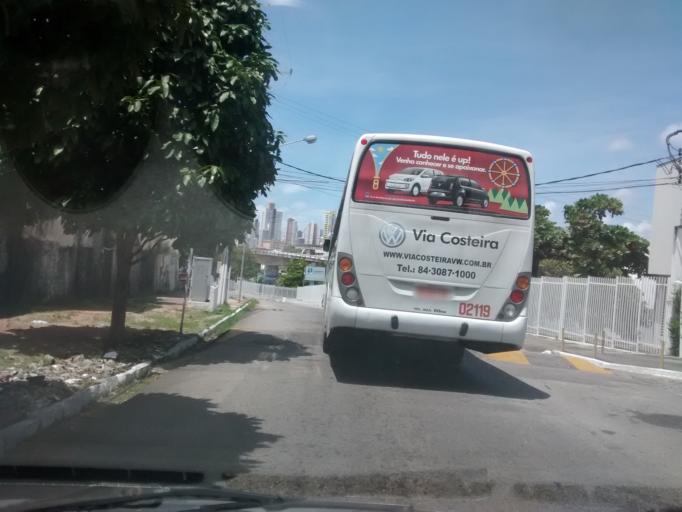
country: BR
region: Rio Grande do Norte
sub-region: Natal
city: Natal
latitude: -5.7890
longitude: -35.2100
